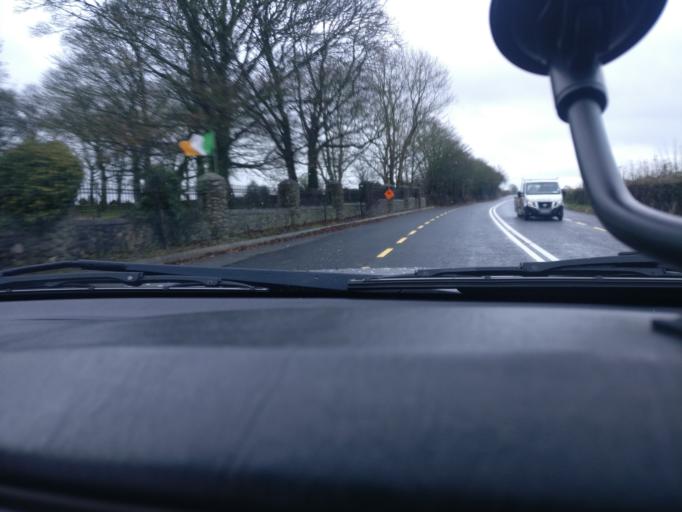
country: IE
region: Leinster
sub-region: An Mhi
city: Longwood
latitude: 53.4257
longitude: -6.8848
